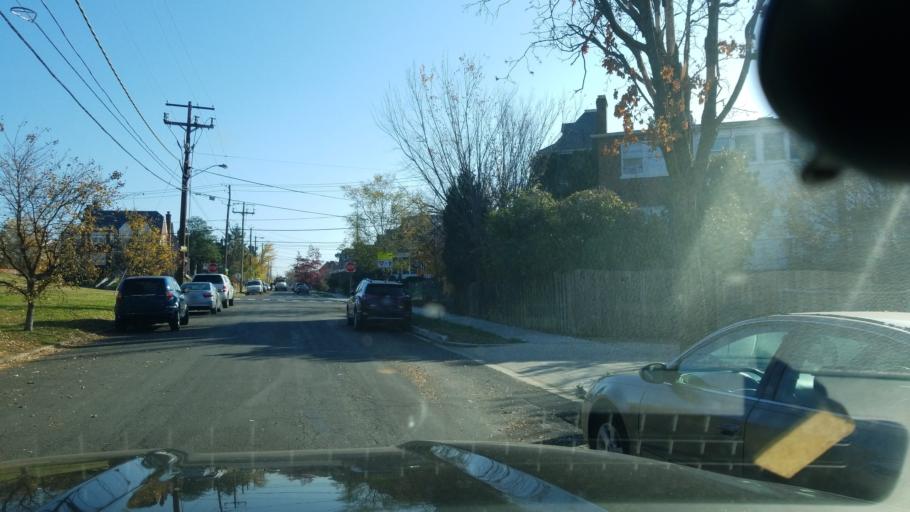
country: US
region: Maryland
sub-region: Montgomery County
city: Takoma Park
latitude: 38.9588
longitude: -77.0143
